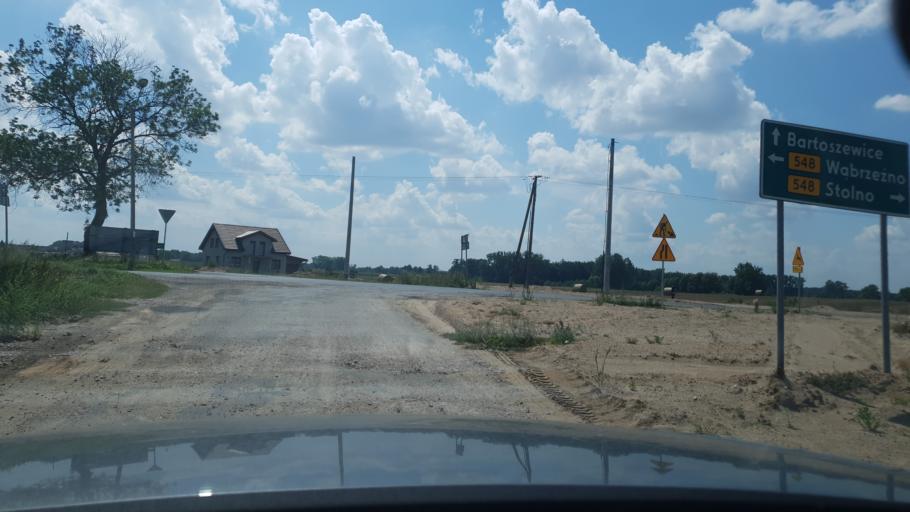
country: PL
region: Kujawsko-Pomorskie
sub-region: Powiat wabrzeski
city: Pluznica
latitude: 53.2909
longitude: 18.8008
